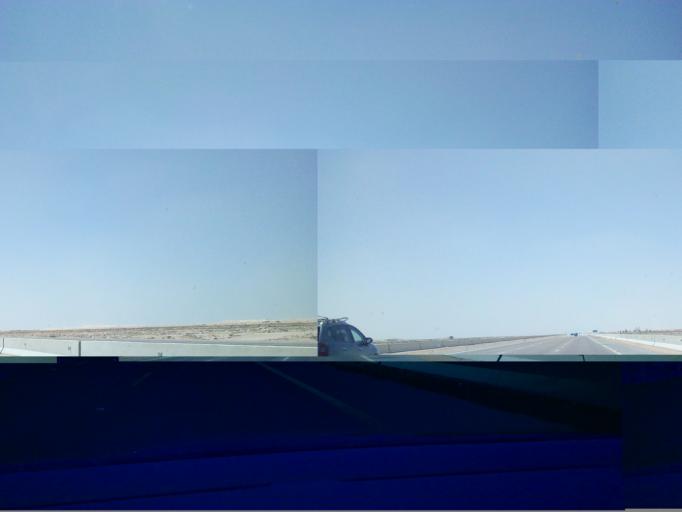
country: EG
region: Al Buhayrah
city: Abu al Matamir
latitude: 30.5903
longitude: 29.8819
